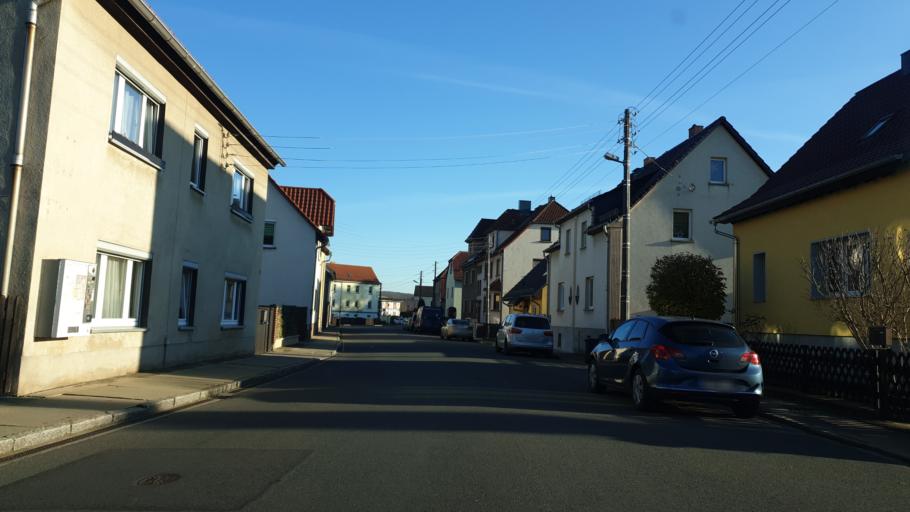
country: DE
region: Thuringia
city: Hartmannsdorf
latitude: 50.9740
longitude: 11.9790
